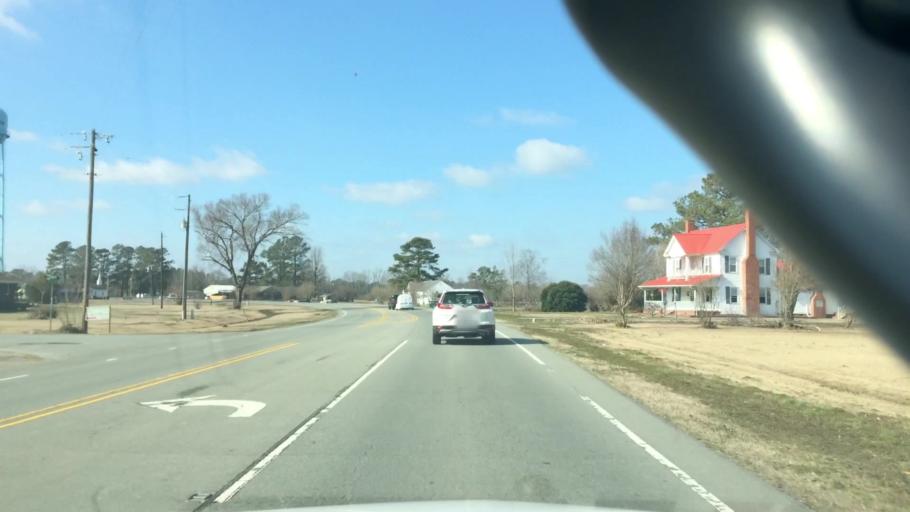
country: US
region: North Carolina
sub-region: Duplin County
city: Beulaville
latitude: 34.8330
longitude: -77.8221
